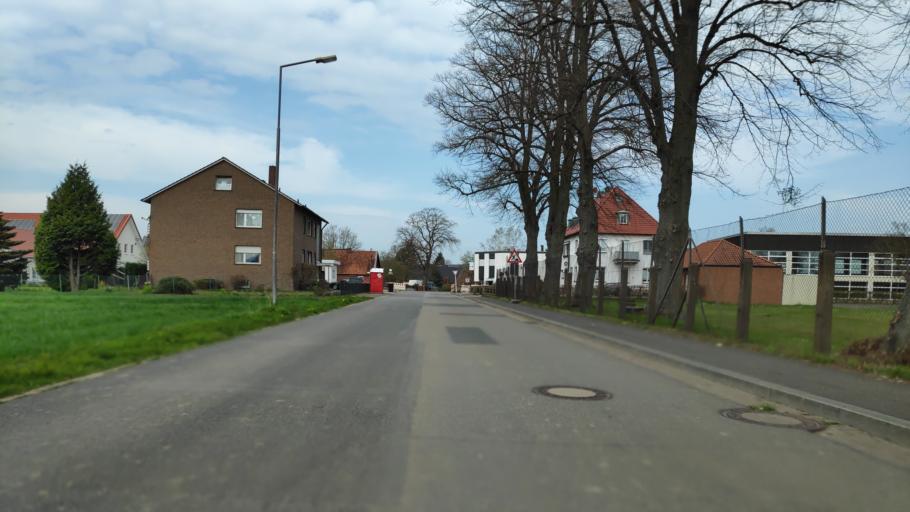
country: DE
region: North Rhine-Westphalia
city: Porta Westfalica
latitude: 52.2668
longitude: 8.9552
